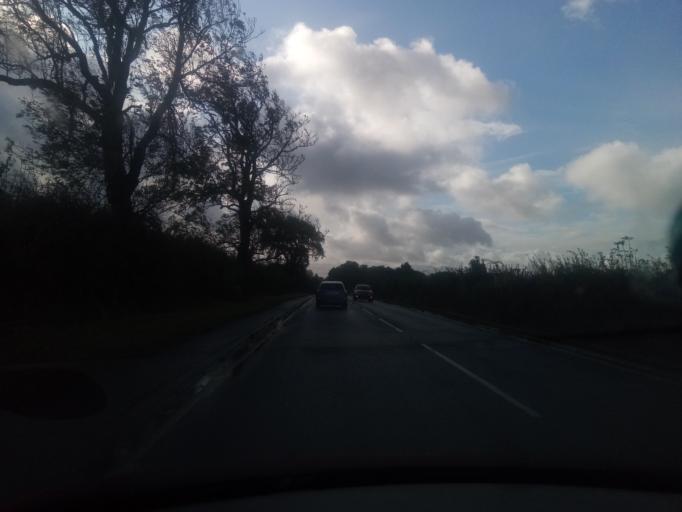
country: GB
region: England
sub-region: Cumbria
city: Carlisle
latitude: 54.9483
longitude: -2.9433
